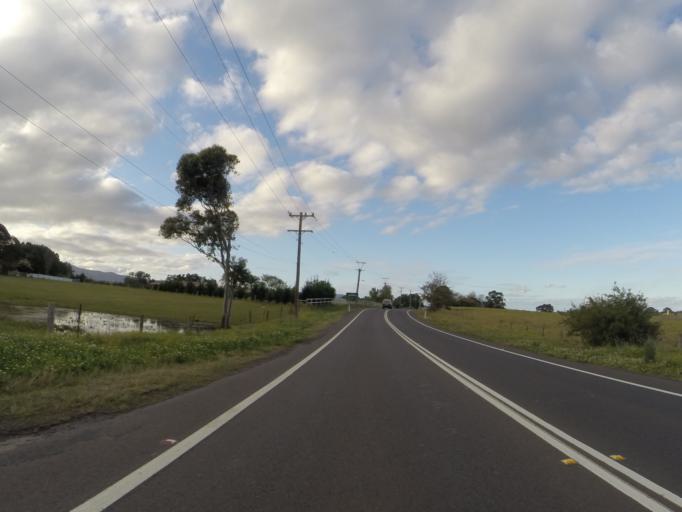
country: AU
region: New South Wales
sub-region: Shellharbour
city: Albion Park Rail
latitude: -34.5679
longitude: 150.7741
